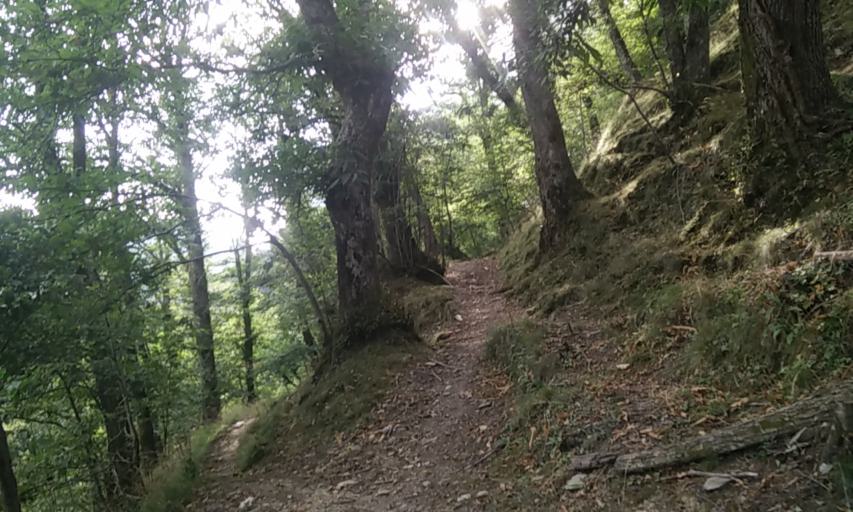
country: IT
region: Tuscany
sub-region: Provincia di Lucca
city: Pontestazzemese
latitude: 43.9991
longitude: 10.3244
